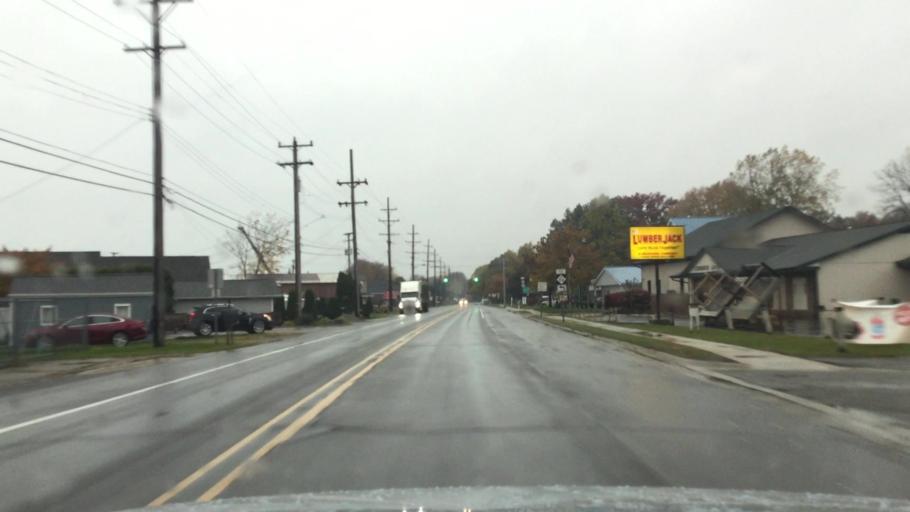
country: US
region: Michigan
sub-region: Saint Clair County
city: Algonac
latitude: 42.6181
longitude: -82.5583
